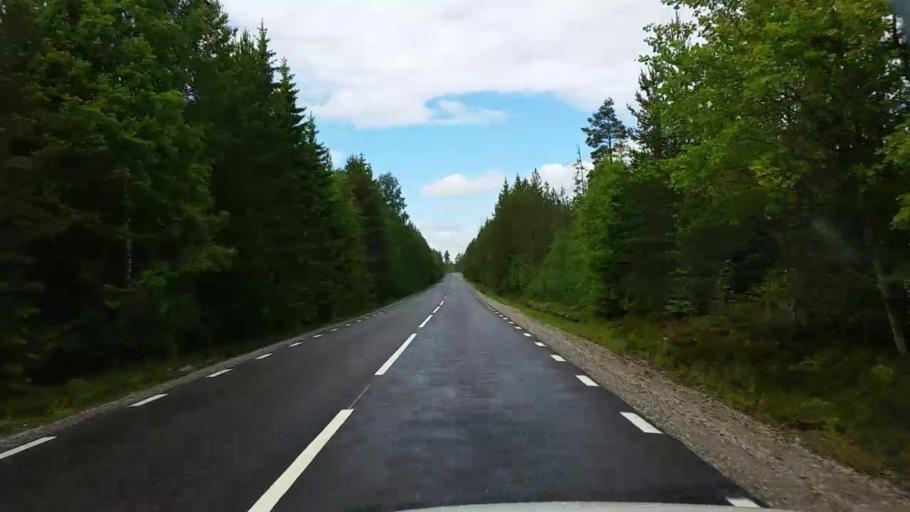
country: SE
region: Gaevleborg
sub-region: Sandvikens Kommun
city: Jarbo
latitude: 60.8717
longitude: 16.4069
